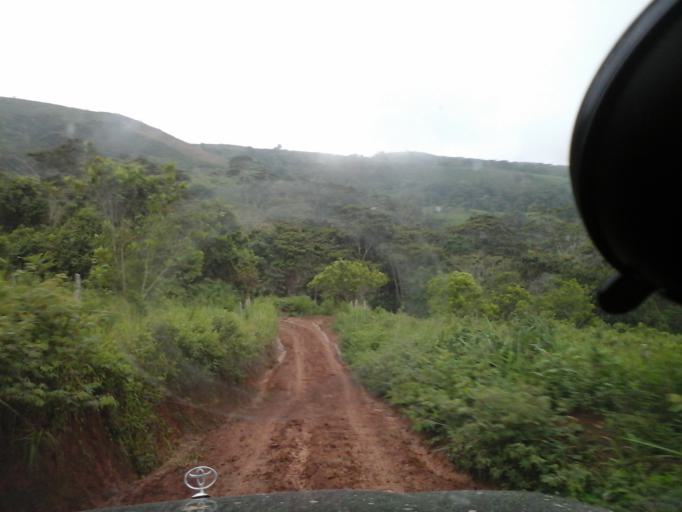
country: CO
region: Cesar
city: Agustin Codazzi
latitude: 9.9592
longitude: -73.0617
